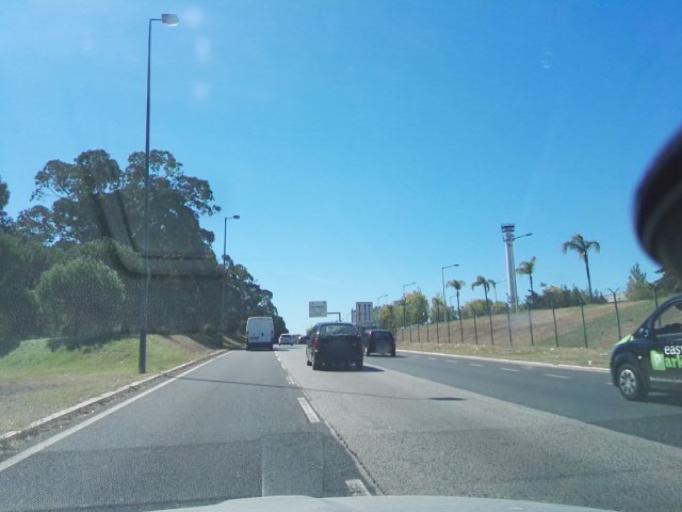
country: PT
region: Lisbon
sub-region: Loures
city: Moscavide
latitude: 38.7771
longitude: -9.1236
